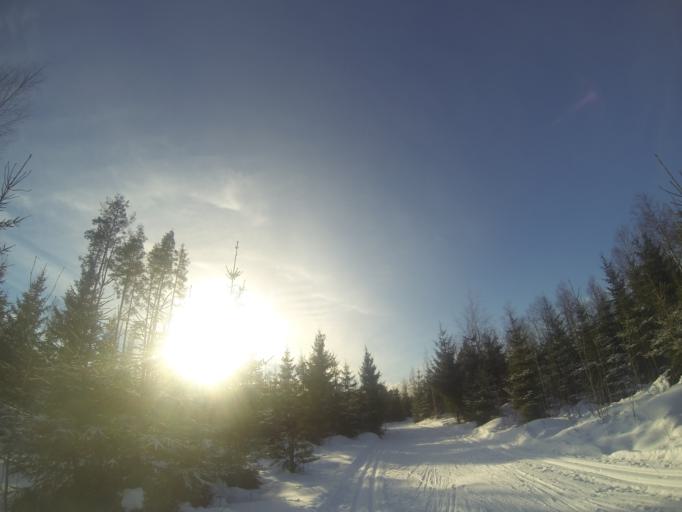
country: FI
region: Southern Savonia
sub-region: Savonlinna
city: Savonlinna
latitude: 61.9042
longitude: 28.9130
